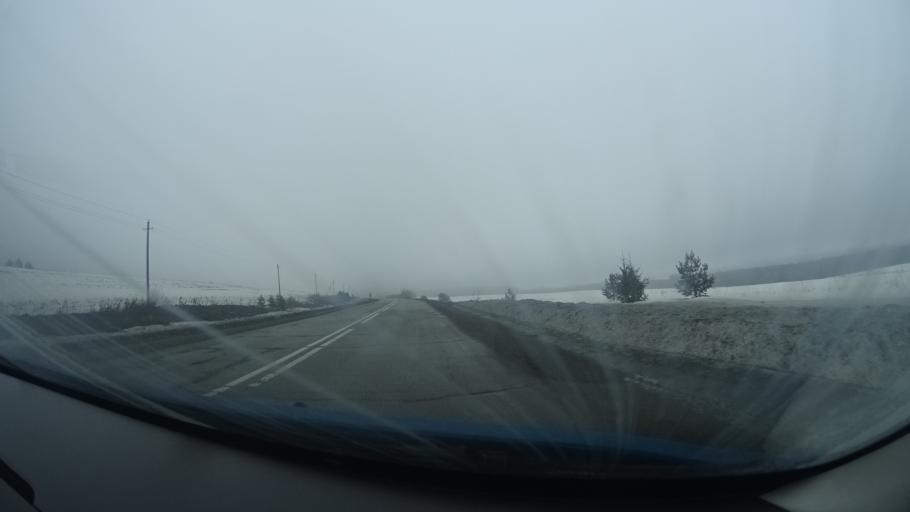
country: RU
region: Perm
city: Kuyeda
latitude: 56.4700
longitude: 55.7382
